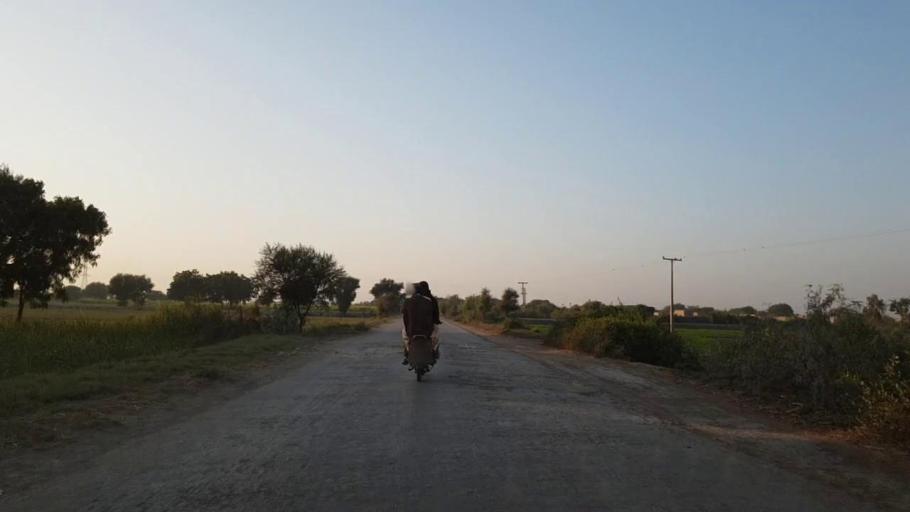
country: PK
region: Sindh
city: Chambar
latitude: 25.2368
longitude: 68.6972
